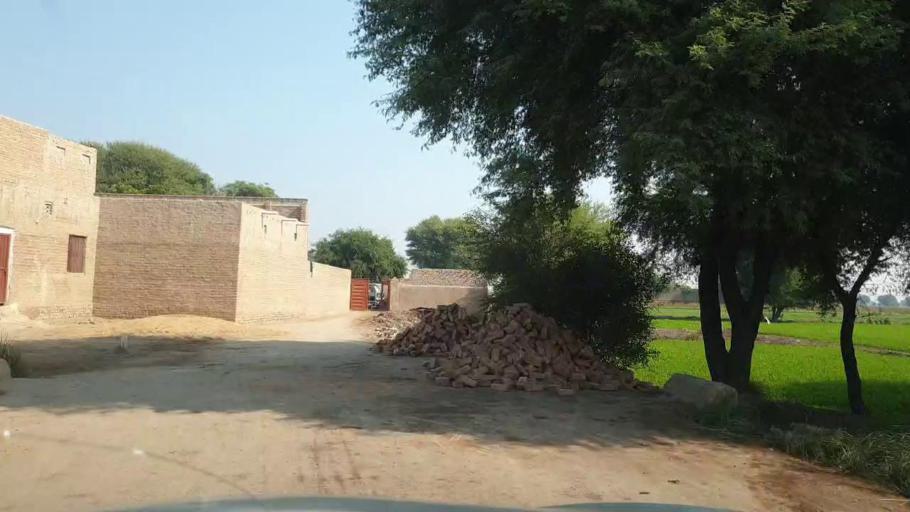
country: PK
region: Sindh
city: Bhan
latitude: 26.5409
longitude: 67.7499
